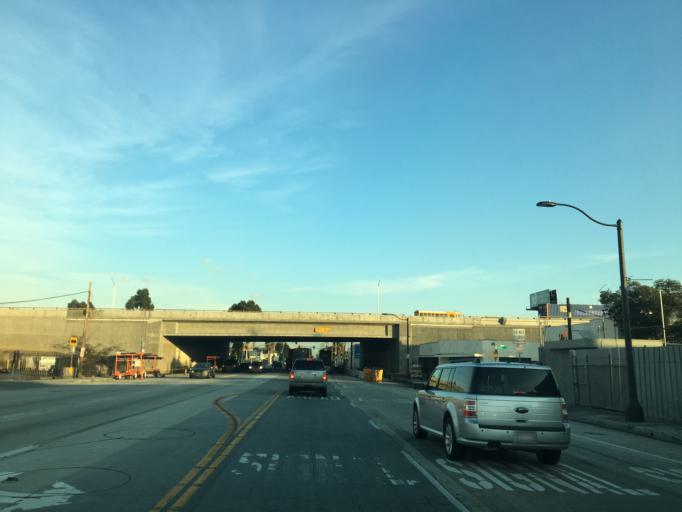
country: US
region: California
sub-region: Los Angeles County
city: Commerce
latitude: 34.0051
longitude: -118.1740
